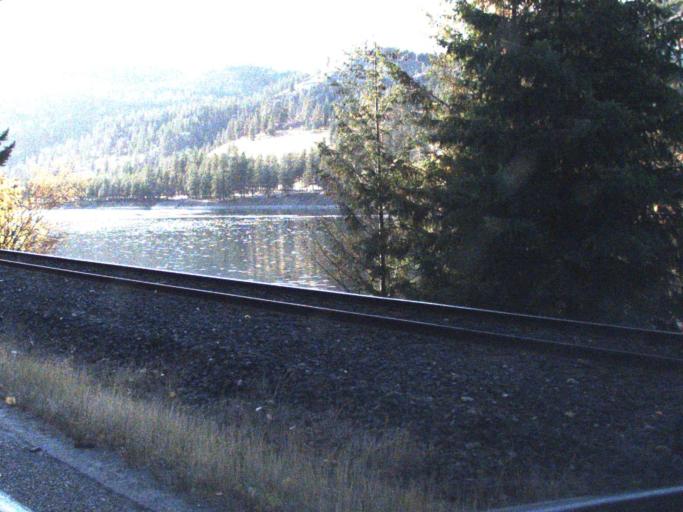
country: US
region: Washington
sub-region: Stevens County
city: Kettle Falls
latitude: 48.7729
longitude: -118.0142
